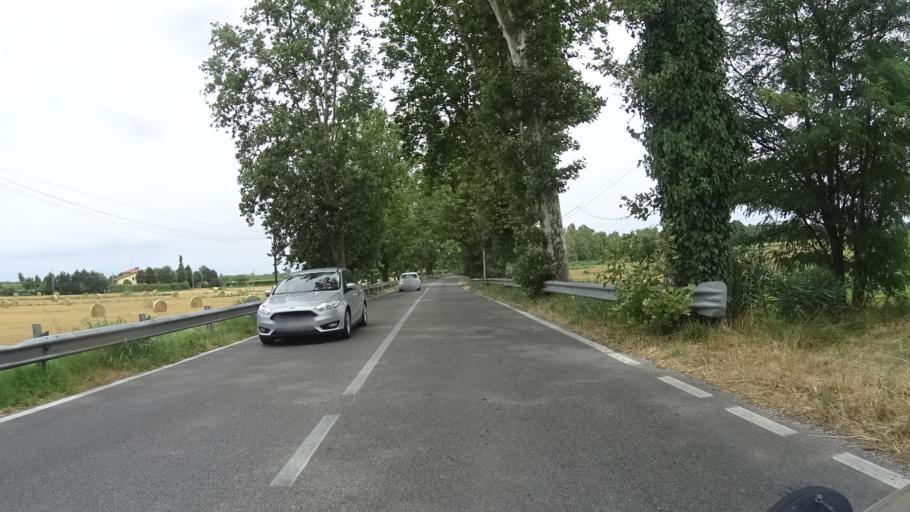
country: IT
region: Veneto
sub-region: Provincia di Venezia
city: La Salute di Livenza
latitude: 45.6927
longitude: 12.8449
